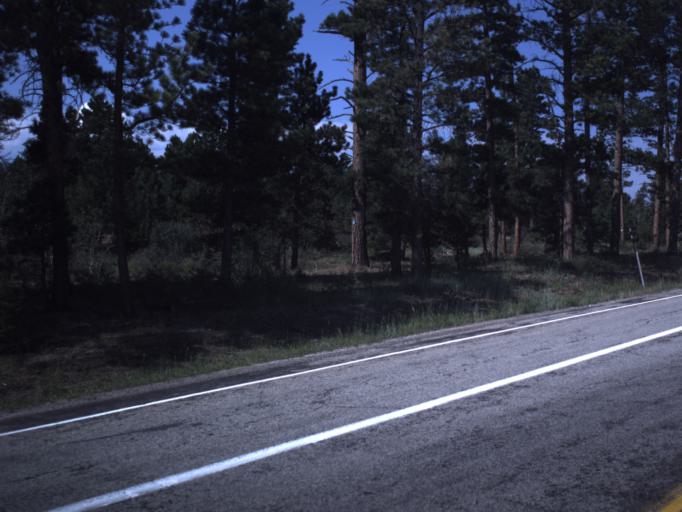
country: US
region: Utah
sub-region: Daggett County
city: Manila
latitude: 40.8609
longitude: -109.5413
